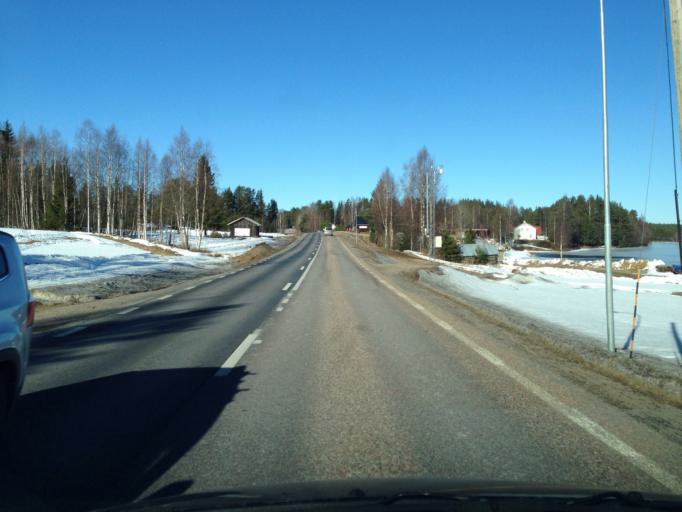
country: SE
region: Gaevleborg
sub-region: Ljusdals Kommun
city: Farila
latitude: 61.9782
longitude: 15.3263
